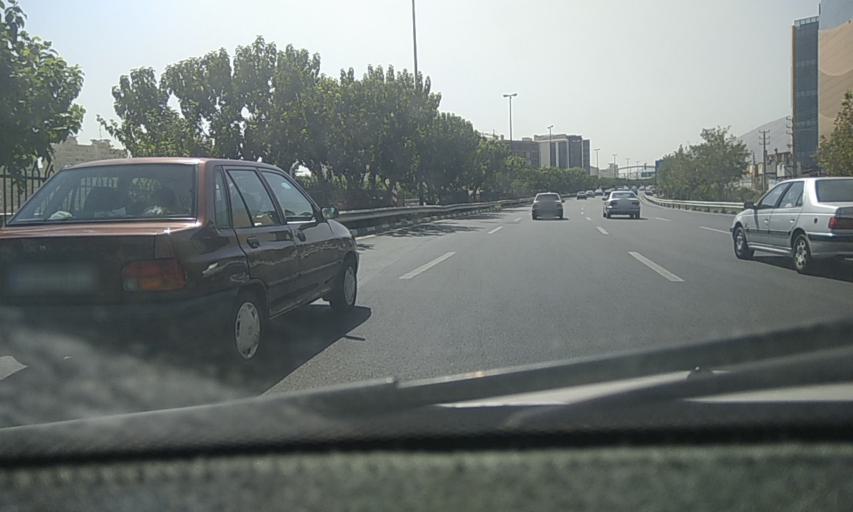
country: IR
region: Tehran
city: Shahr-e Qods
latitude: 35.7567
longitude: 51.2226
